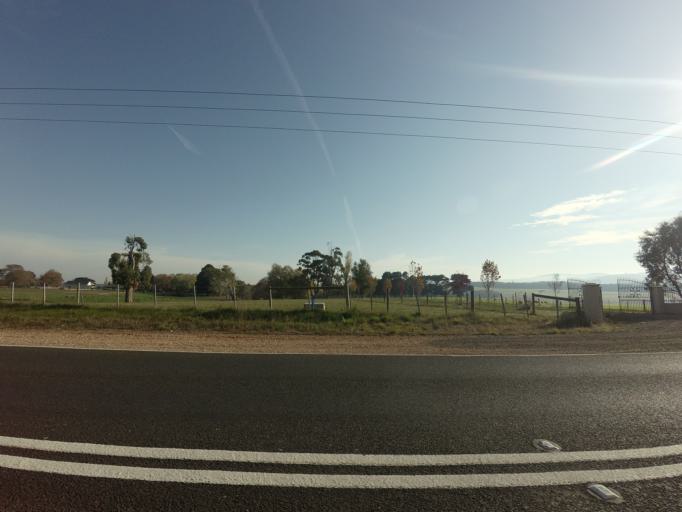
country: AU
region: Tasmania
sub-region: Launceston
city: Summerhill
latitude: -41.5257
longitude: 147.0274
